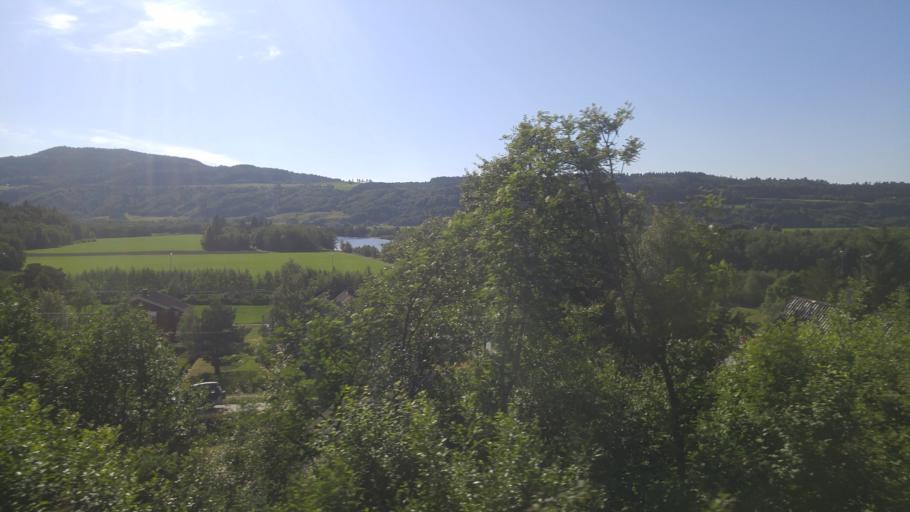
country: NO
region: Sor-Trondelag
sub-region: Melhus
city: Melhus
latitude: 63.2587
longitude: 10.2873
